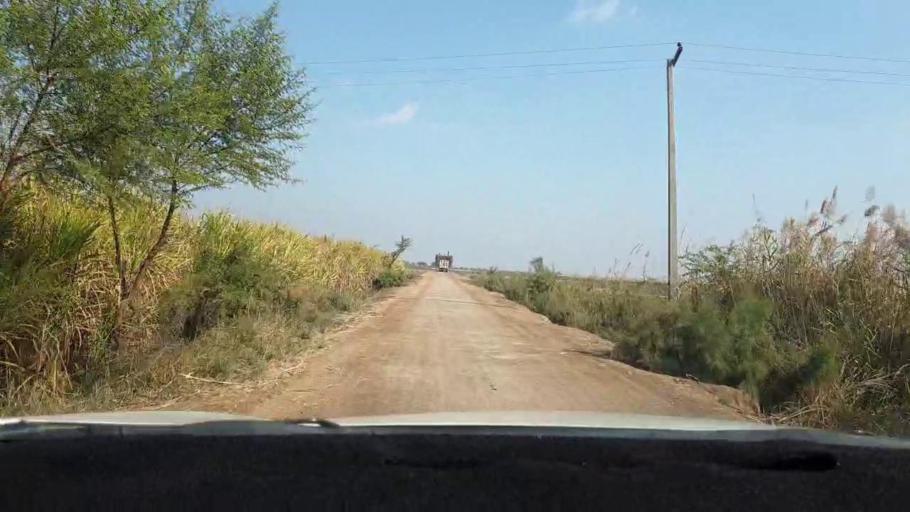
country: PK
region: Sindh
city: Berani
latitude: 25.8075
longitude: 68.8365
